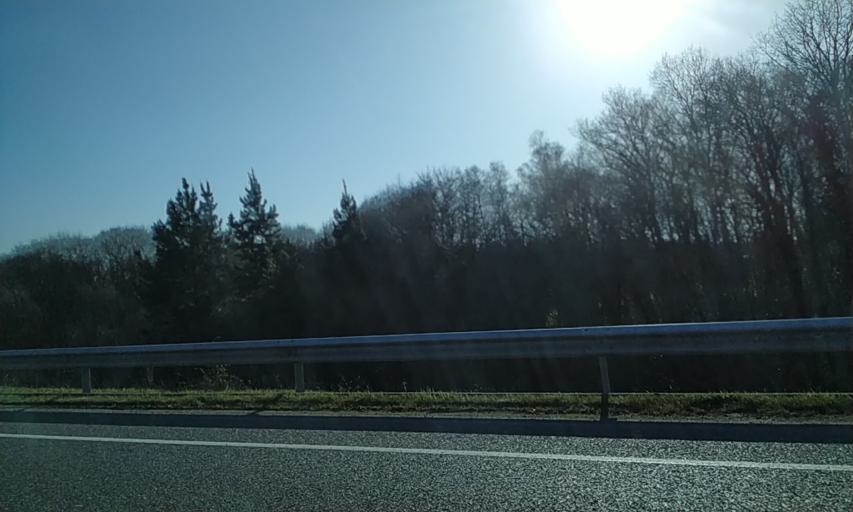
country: ES
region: Galicia
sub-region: Provincia de Lugo
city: Lugo
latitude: 43.0373
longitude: -7.5218
